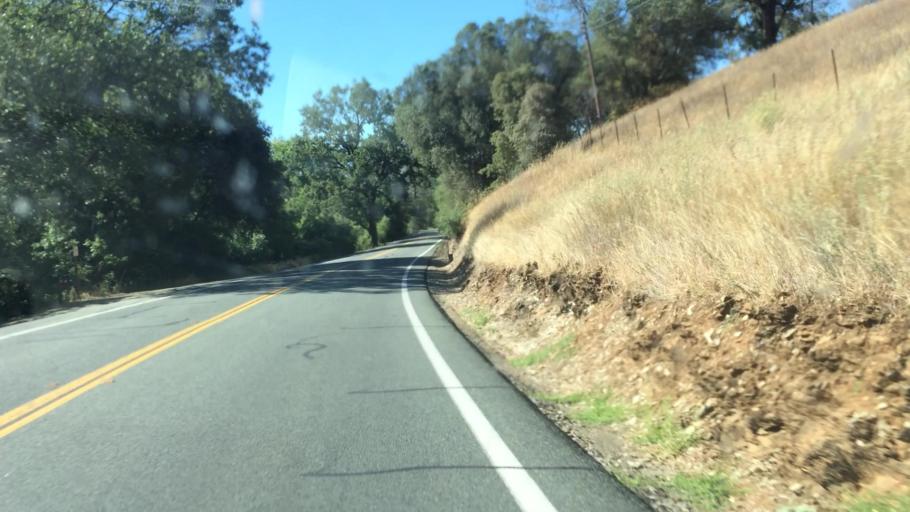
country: US
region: California
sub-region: Amador County
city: Plymouth
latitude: 38.5493
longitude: -120.8488
